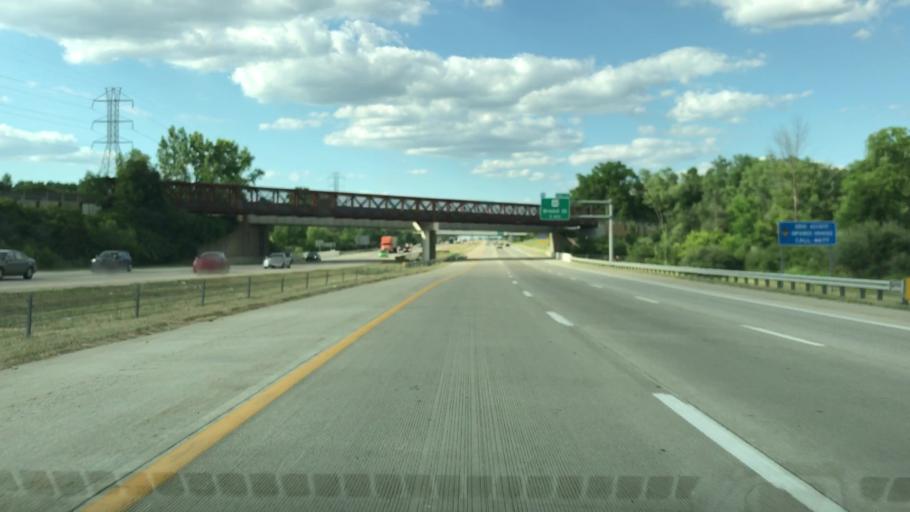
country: US
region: Ohio
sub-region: Franklin County
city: Lincoln Village
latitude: 39.9348
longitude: -83.1236
